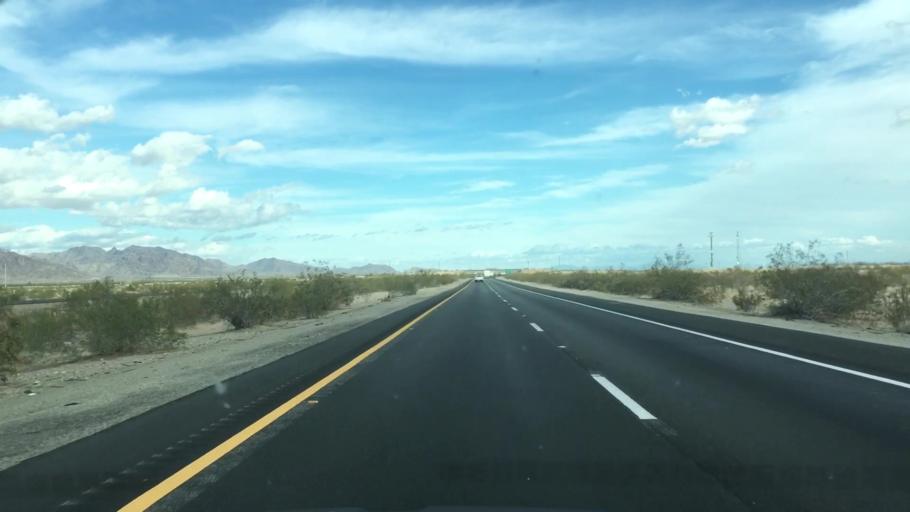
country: US
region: California
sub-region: Riverside County
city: Mesa Verde
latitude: 33.6069
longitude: -114.9138
